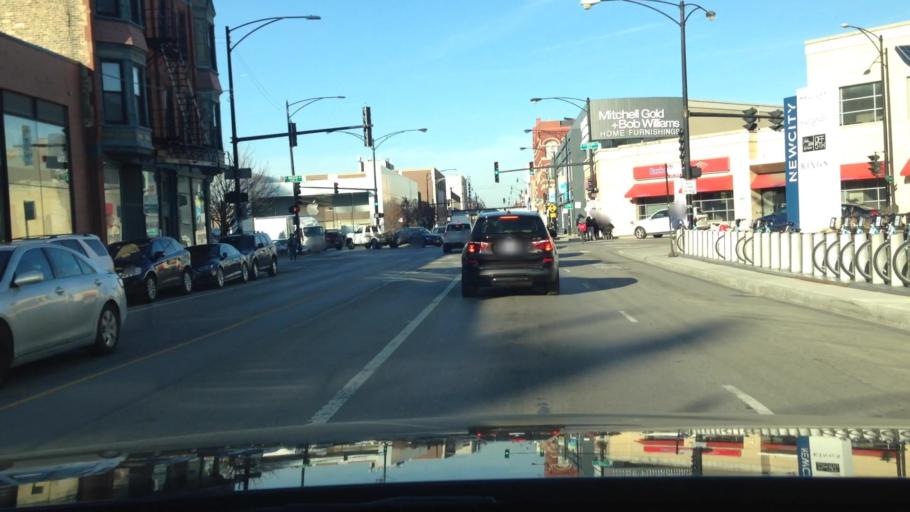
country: US
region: Illinois
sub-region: Cook County
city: Chicago
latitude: 41.9094
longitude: -87.6482
